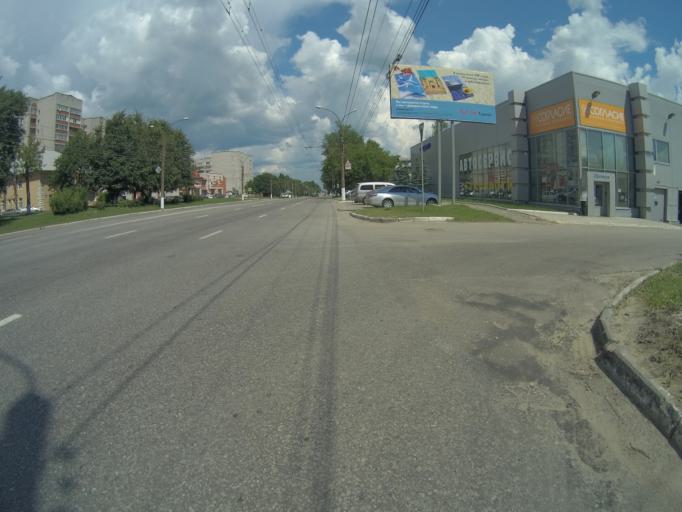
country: RU
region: Vladimir
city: Bogolyubovo
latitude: 56.1671
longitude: 40.4834
